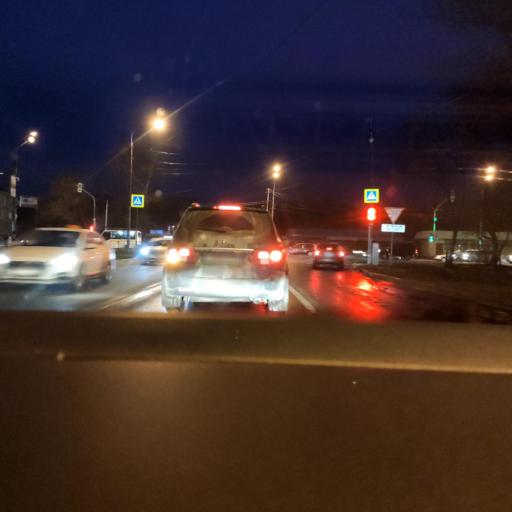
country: RU
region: Moscow
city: Vostochnyy
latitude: 55.8218
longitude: 37.8702
